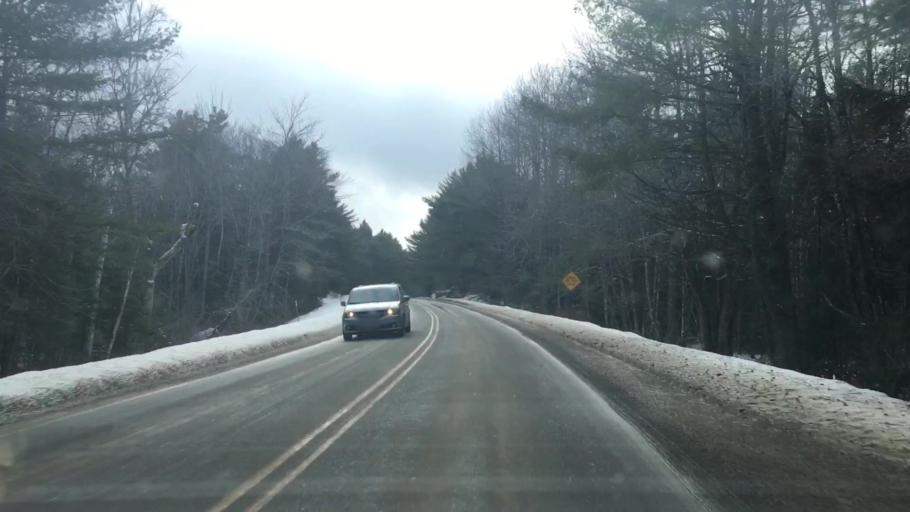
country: US
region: Maine
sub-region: Washington County
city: Calais
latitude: 45.0454
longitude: -67.3278
